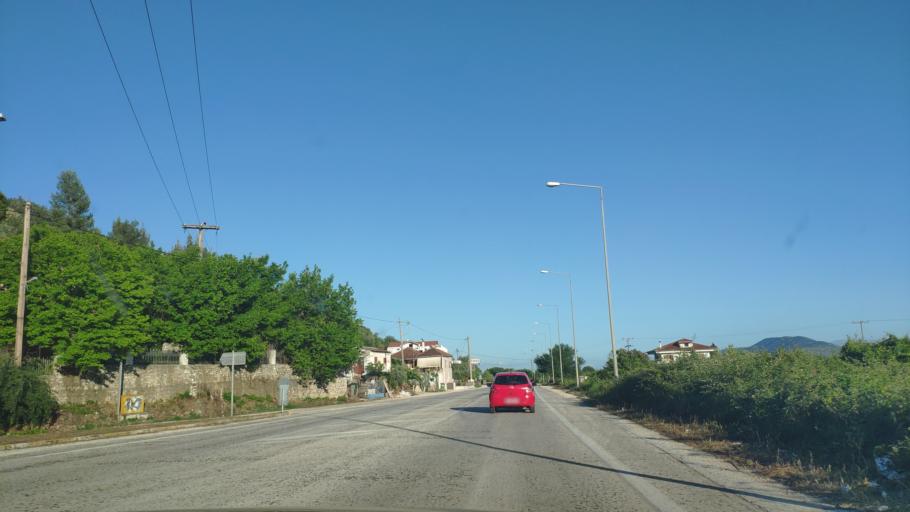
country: GR
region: Epirus
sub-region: Nomos Prevezis
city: Louros
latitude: 39.1772
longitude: 20.7891
